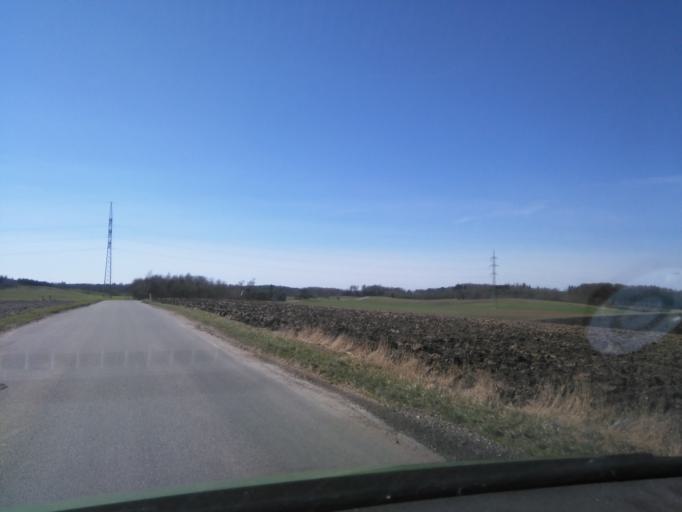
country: DK
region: Central Jutland
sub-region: Arhus Kommune
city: Trige
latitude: 56.2421
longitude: 10.1915
